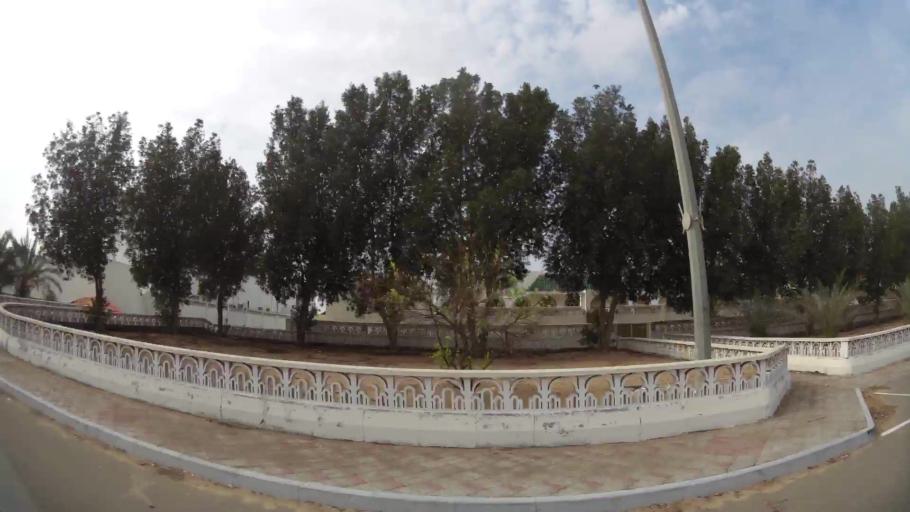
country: AE
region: Abu Dhabi
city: Abu Dhabi
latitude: 24.6486
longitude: 54.7302
